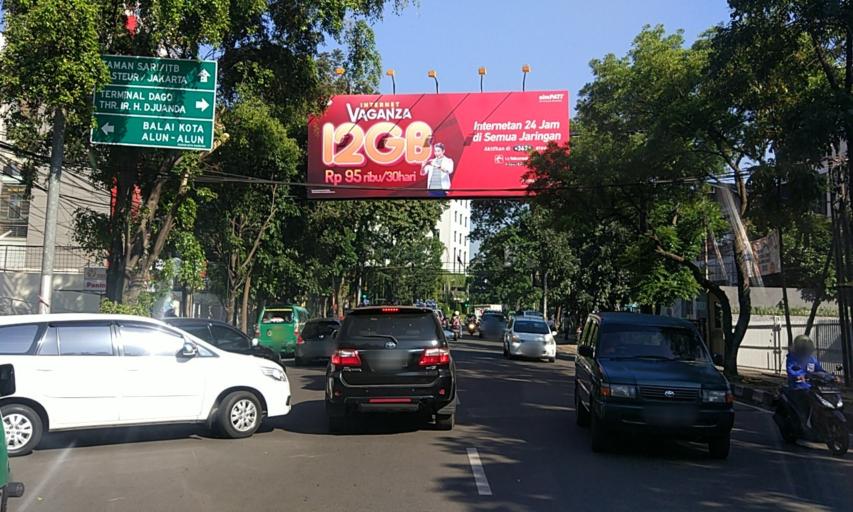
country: ID
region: West Java
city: Bandung
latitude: -6.9006
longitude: 107.6135
